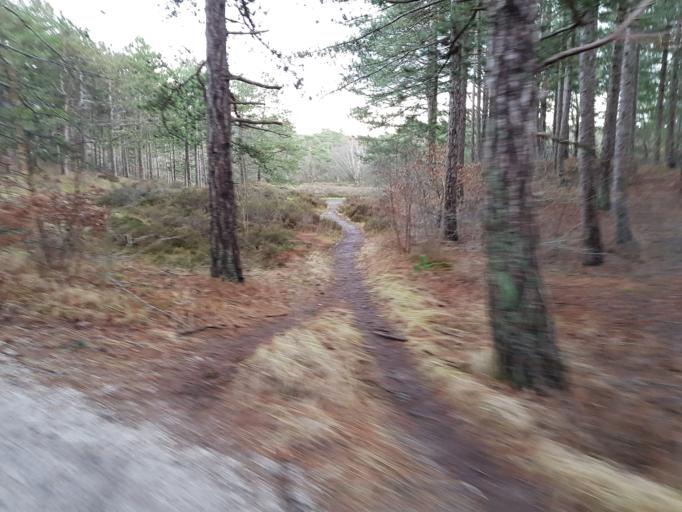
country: NL
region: North Holland
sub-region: Gemeente Bergen
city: Egmond aan Zee
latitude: 52.6918
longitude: 4.6644
